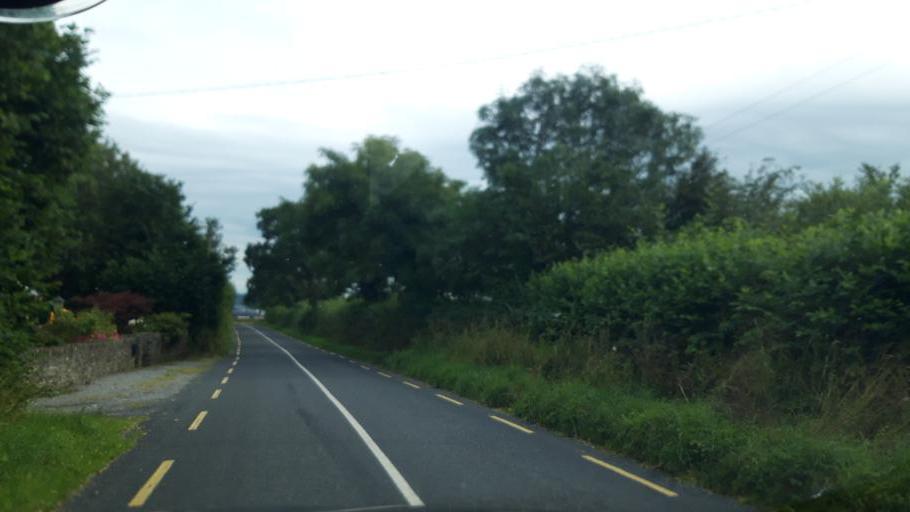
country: IE
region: Leinster
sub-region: Kilkenny
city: Ballyragget
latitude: 52.7517
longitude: -7.3918
